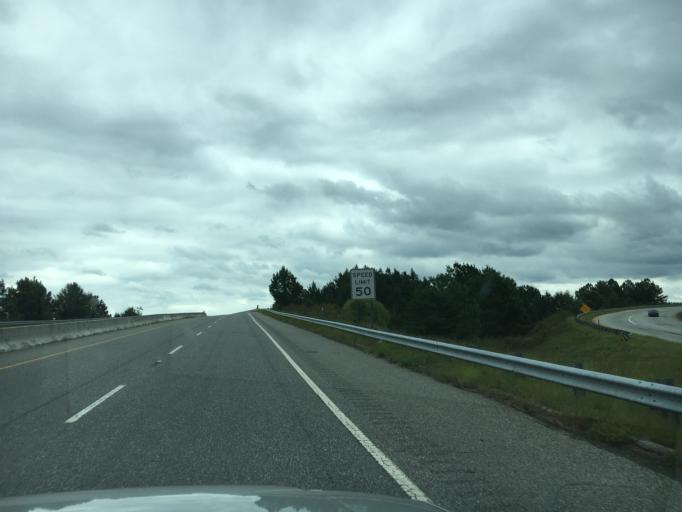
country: US
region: South Carolina
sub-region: Greenville County
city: Mauldin
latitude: 34.7541
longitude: -82.2905
